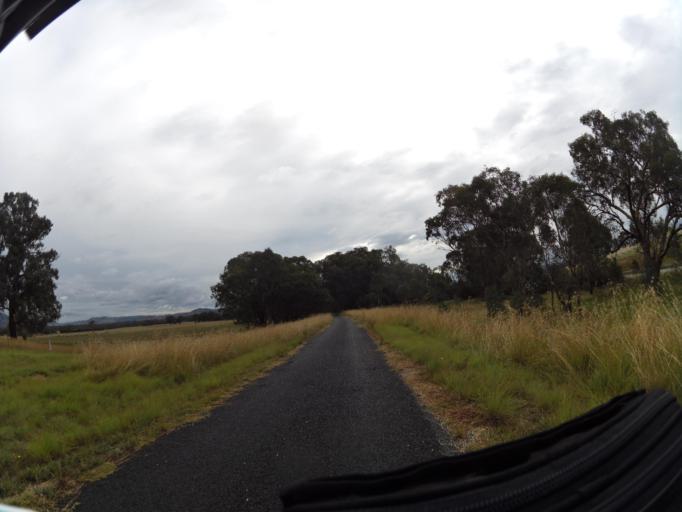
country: AU
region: New South Wales
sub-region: Albury Municipality
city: East Albury
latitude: -36.1397
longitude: 146.9900
